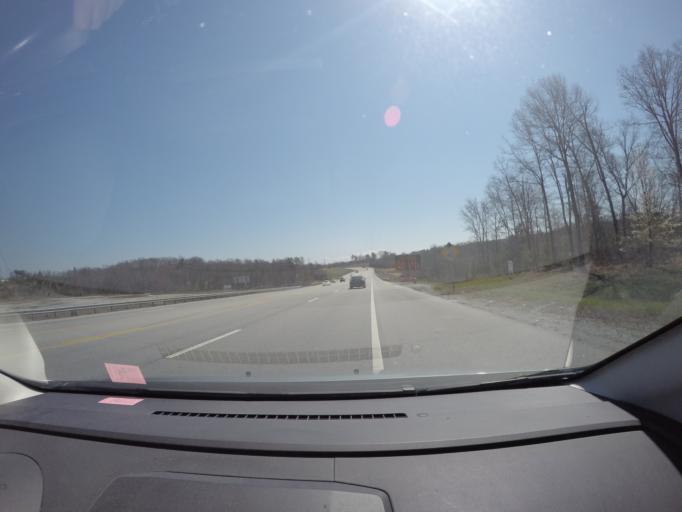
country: US
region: Tennessee
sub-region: Hamilton County
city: Harrison
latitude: 35.0728
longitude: -85.1094
